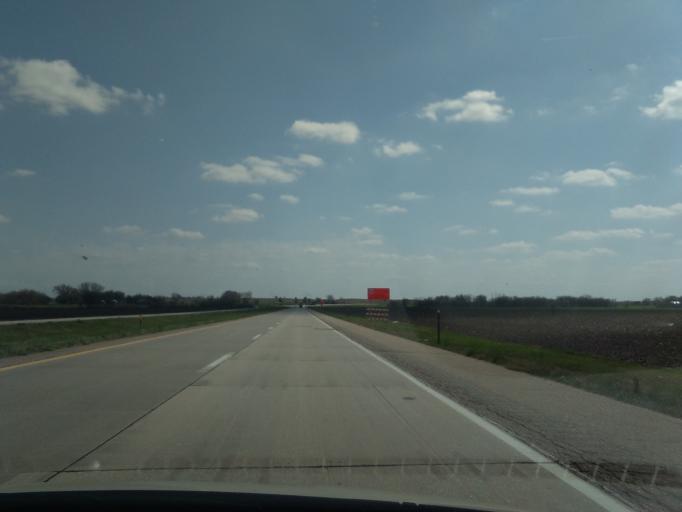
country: US
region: Nebraska
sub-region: Thayer County
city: Hebron
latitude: 40.1538
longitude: -97.5709
